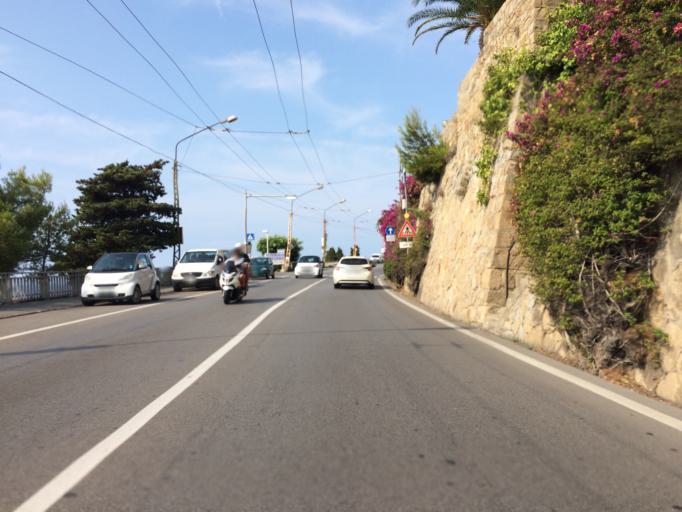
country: IT
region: Liguria
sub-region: Provincia di Imperia
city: Ospedaletti
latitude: 43.7971
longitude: 7.7393
